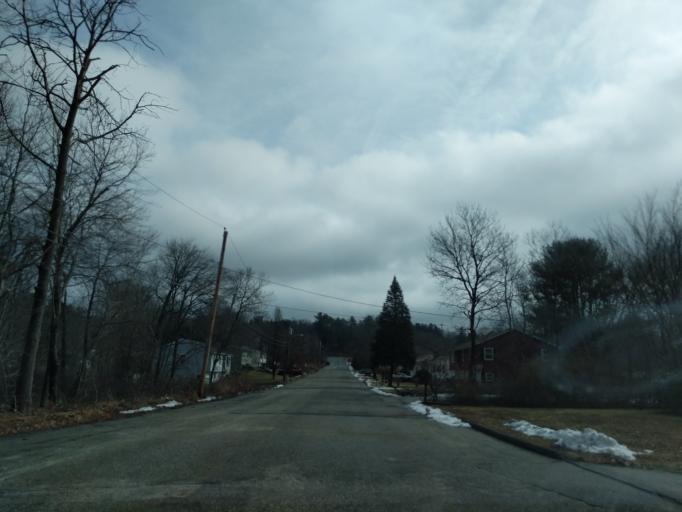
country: US
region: Massachusetts
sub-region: Worcester County
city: Webster
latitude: 42.0773
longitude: -71.8738
